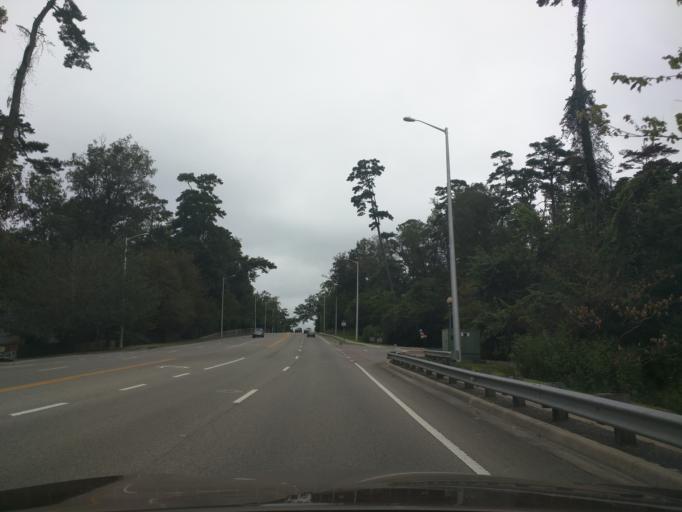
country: US
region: Florida
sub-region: Leon County
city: Tallahassee
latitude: 30.4420
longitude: -84.2334
